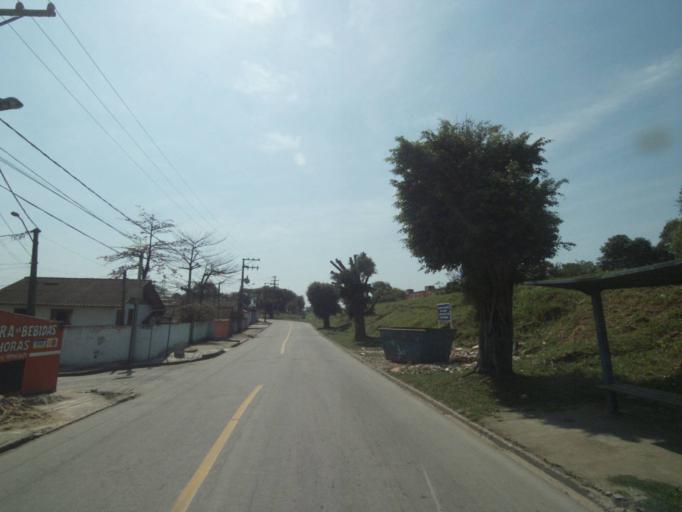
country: BR
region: Parana
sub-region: Paranagua
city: Paranagua
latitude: -25.5479
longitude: -48.5527
